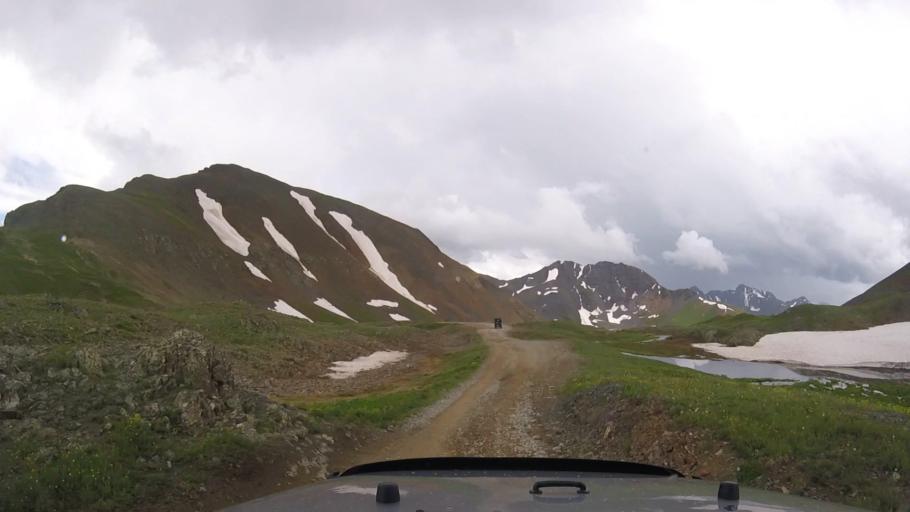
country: US
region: Colorado
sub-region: Ouray County
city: Ouray
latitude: 37.9187
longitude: -107.6290
